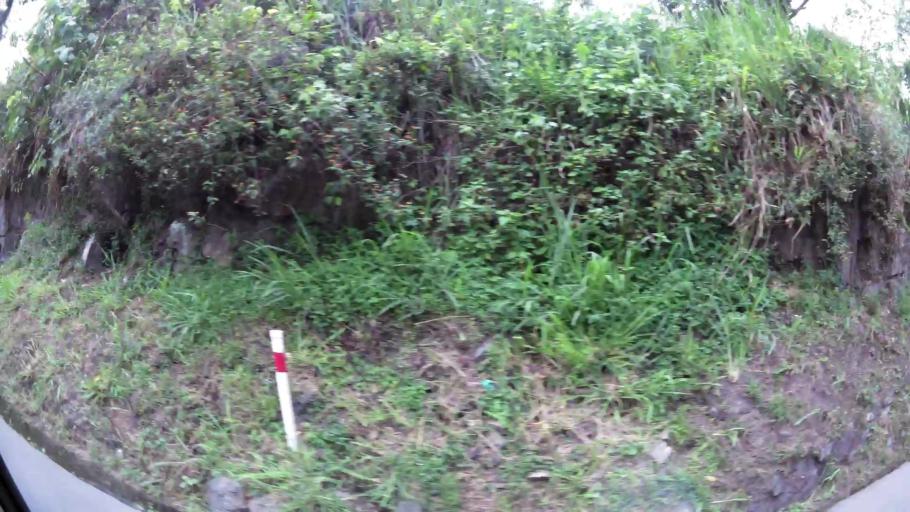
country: EC
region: Santo Domingo de los Tsachilas
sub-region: Canton Santo Domingo de los Colorados
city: Santo Domingo de los Colorados
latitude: -0.2847
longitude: -79.0685
